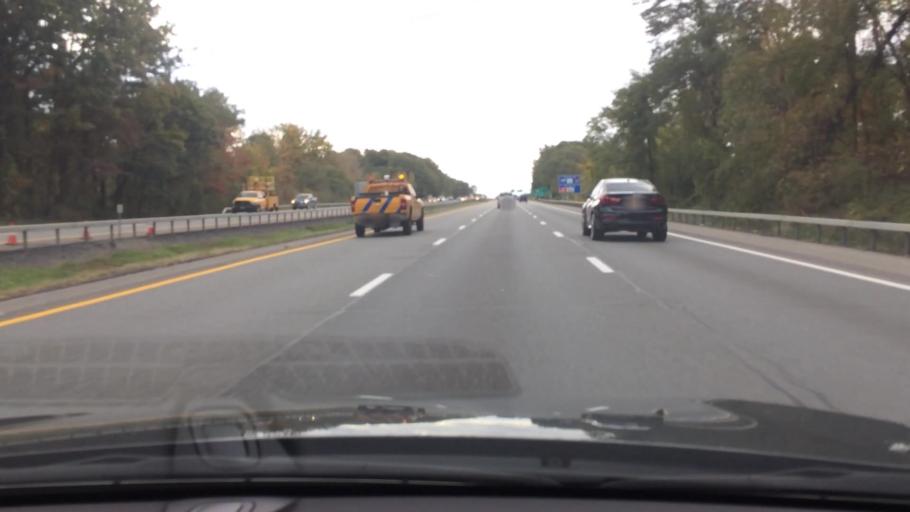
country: US
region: New York
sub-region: Saratoga County
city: Country Knolls
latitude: 42.8710
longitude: -73.7769
